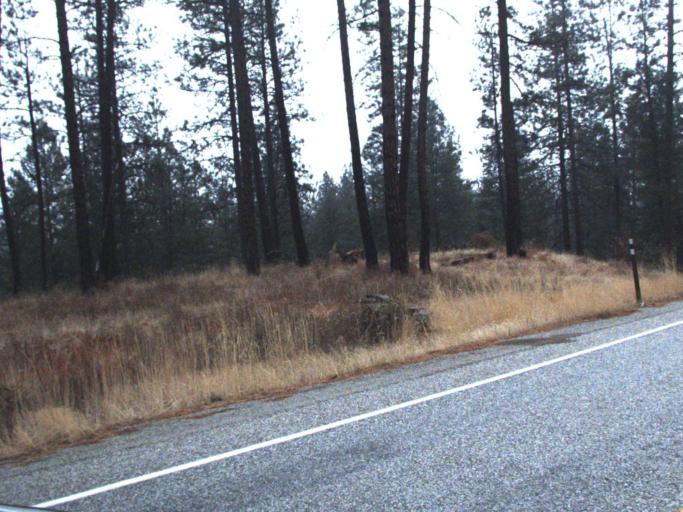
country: US
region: Washington
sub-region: Stevens County
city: Kettle Falls
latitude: 48.7612
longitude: -118.1391
